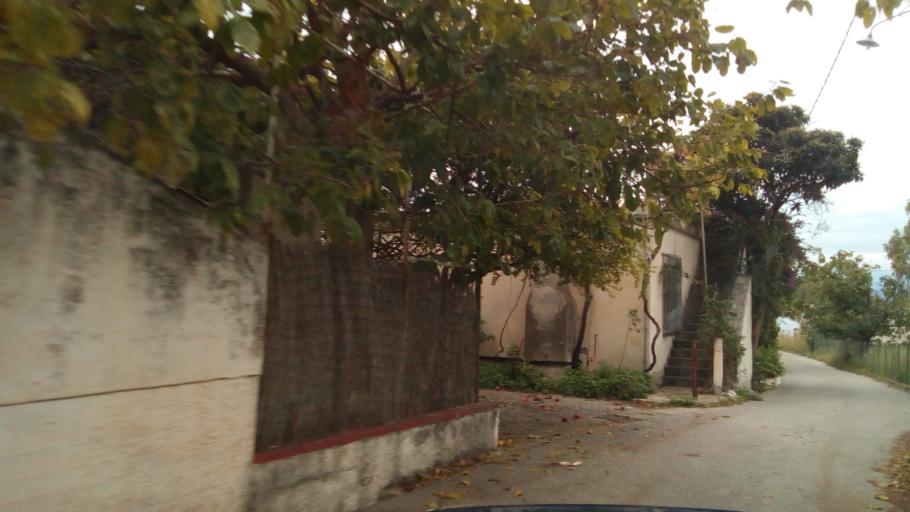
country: GR
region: West Greece
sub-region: Nomos Achaias
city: Kamarai
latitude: 38.3913
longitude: 22.0573
